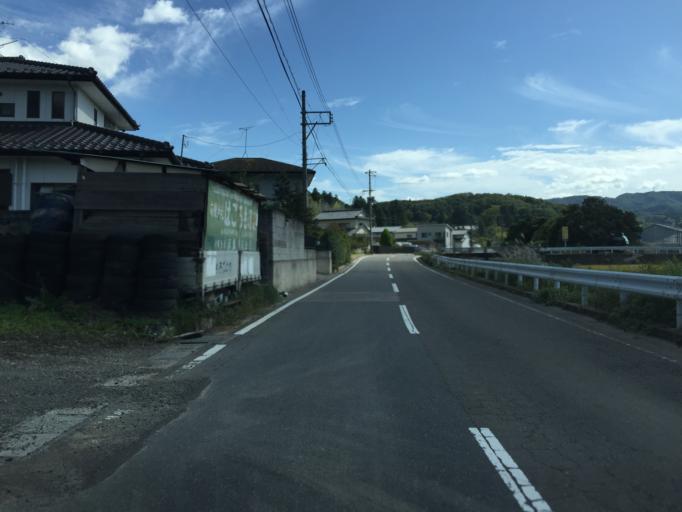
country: JP
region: Fukushima
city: Fukushima-shi
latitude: 37.7760
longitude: 140.5128
